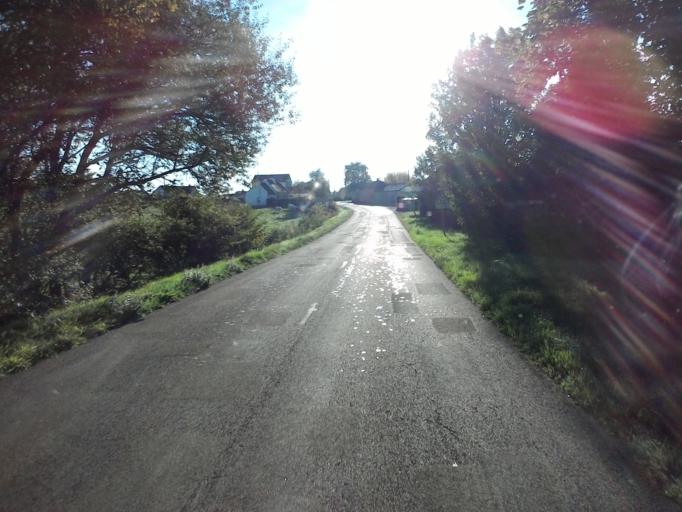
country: FR
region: Bourgogne
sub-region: Departement de la Cote-d'Or
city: Saulieu
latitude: 47.2756
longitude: 4.2221
